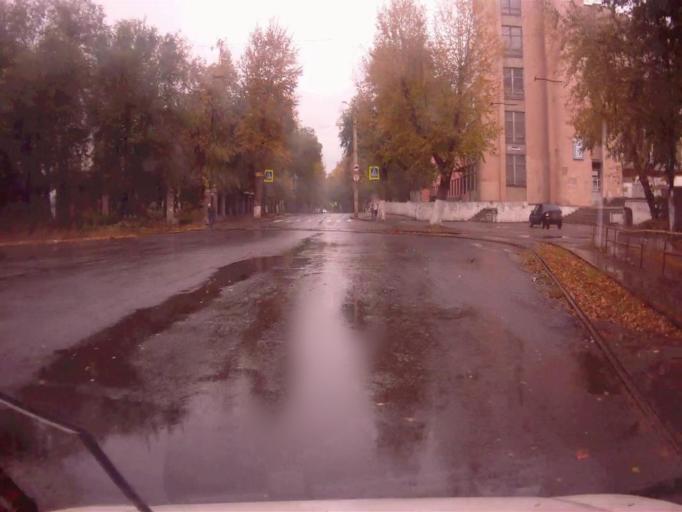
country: RU
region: Chelyabinsk
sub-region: Gorod Chelyabinsk
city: Chelyabinsk
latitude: 55.1911
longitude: 61.4124
